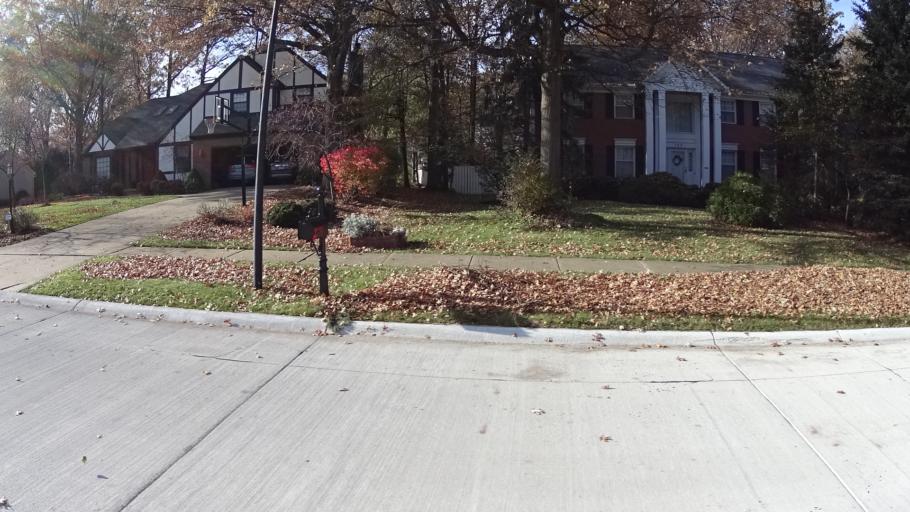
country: US
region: Ohio
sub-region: Lorain County
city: Avon Lake
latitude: 41.5044
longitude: -81.9810
